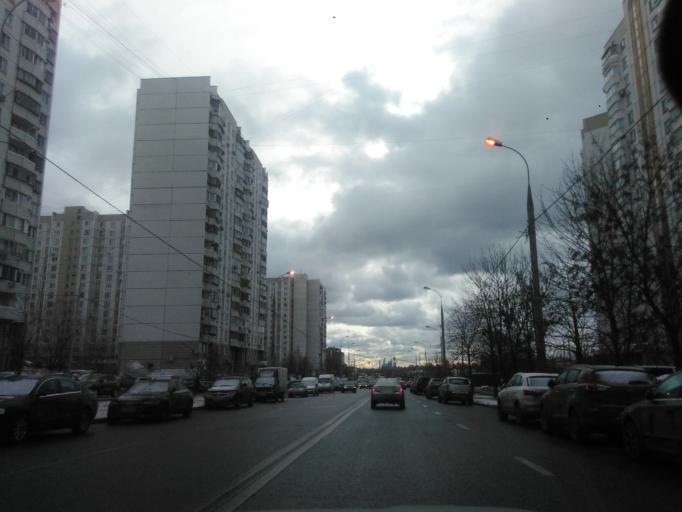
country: RU
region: Moskovskaya
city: Pavshino
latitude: 55.8439
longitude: 37.3511
